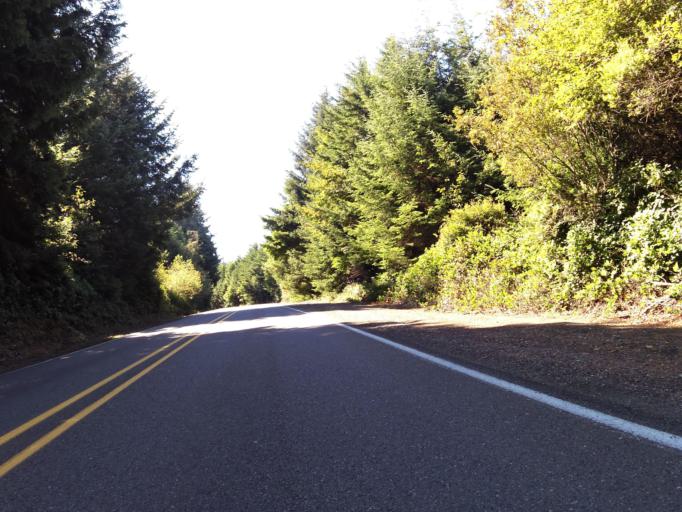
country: US
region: Oregon
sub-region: Coos County
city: Barview
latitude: 43.2414
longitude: -124.3366
